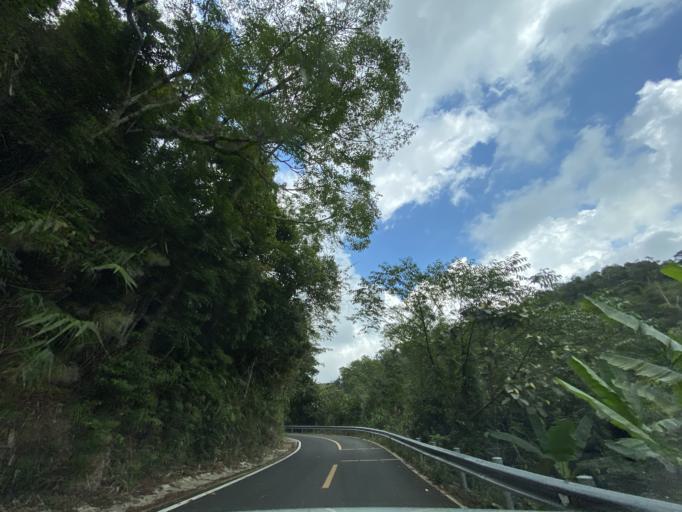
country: CN
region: Hainan
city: Benhao
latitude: 18.6919
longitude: 109.8803
